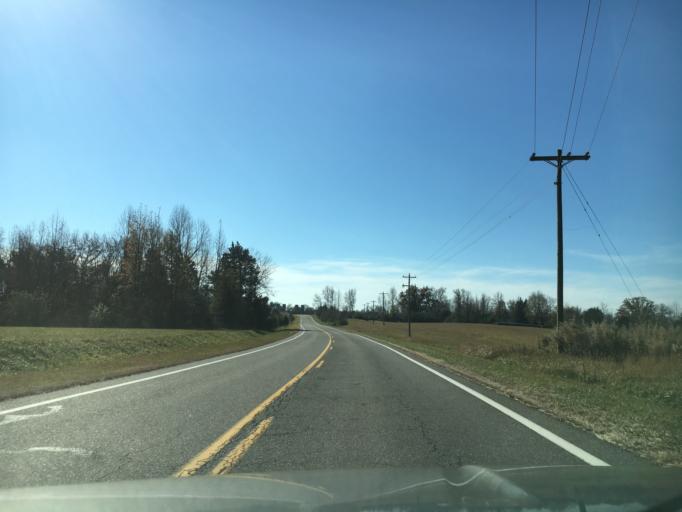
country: US
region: Virginia
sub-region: Cumberland County
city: Cumberland
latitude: 37.6002
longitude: -78.1706
